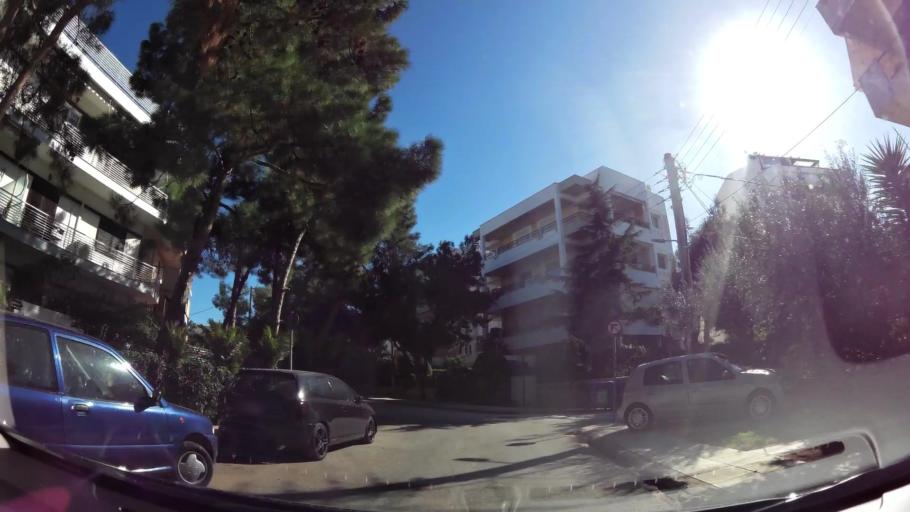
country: GR
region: Attica
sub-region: Nomarchia Athinas
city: Glyfada
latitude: 37.8516
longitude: 23.7598
